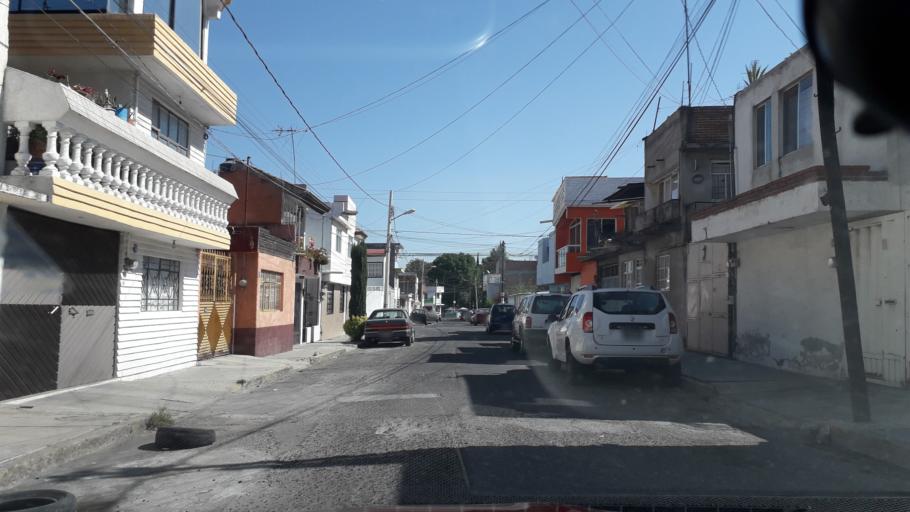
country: MX
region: Puebla
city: Puebla
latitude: 19.0768
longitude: -98.2121
